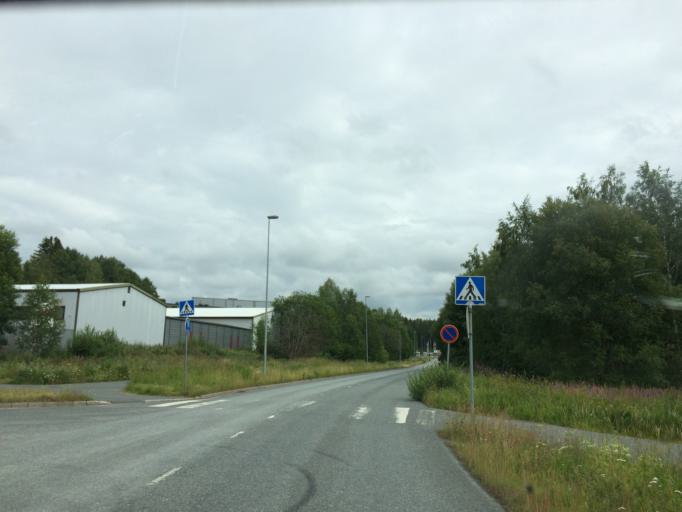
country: FI
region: Haeme
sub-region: Haemeenlinna
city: Haemeenlinna
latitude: 60.9771
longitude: 24.5166
